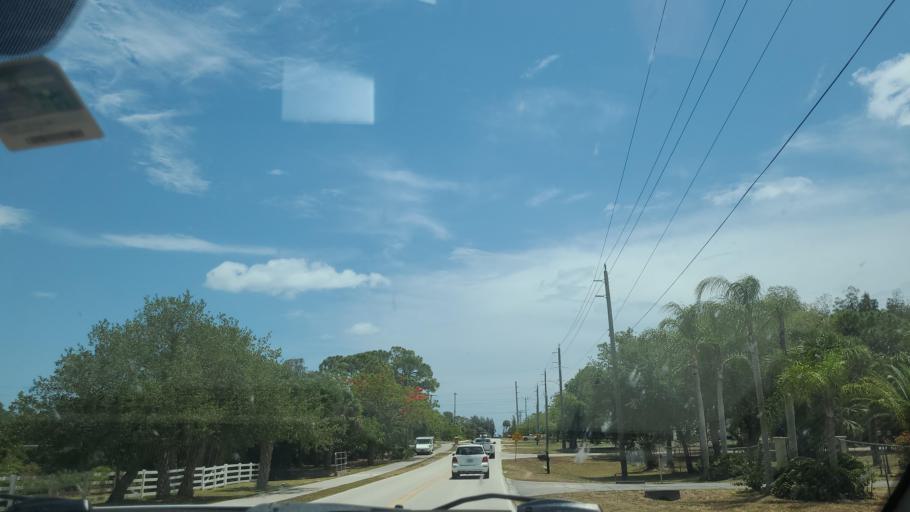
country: US
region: Florida
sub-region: Brevard County
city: Grant-Valkaria
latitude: 27.9638
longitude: -80.5496
